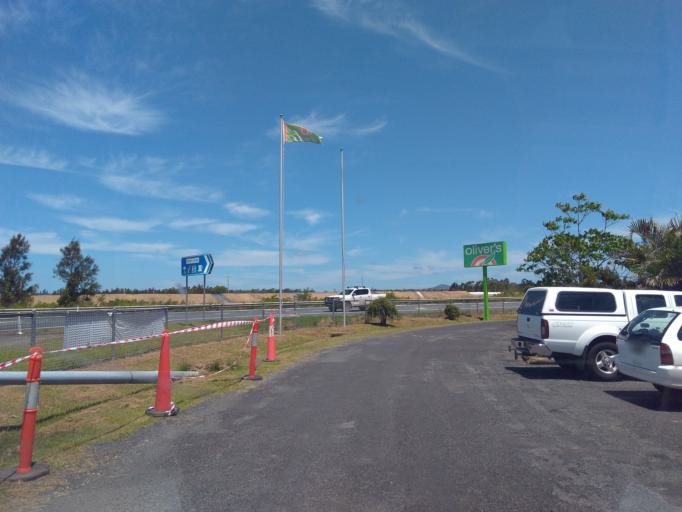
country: AU
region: New South Wales
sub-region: Clarence Valley
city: Maclean
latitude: -29.4723
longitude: 153.2052
